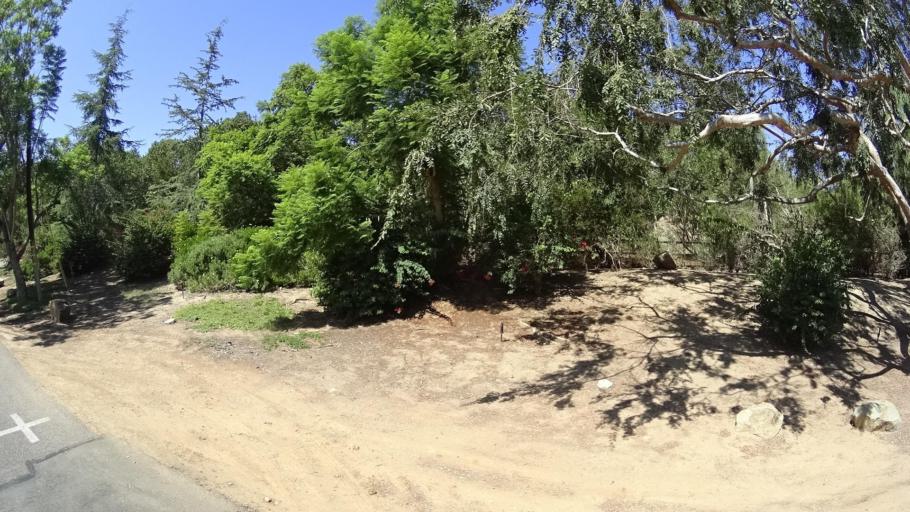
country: US
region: California
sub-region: San Diego County
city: Rancho Santa Fe
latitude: 33.0188
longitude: -117.1829
